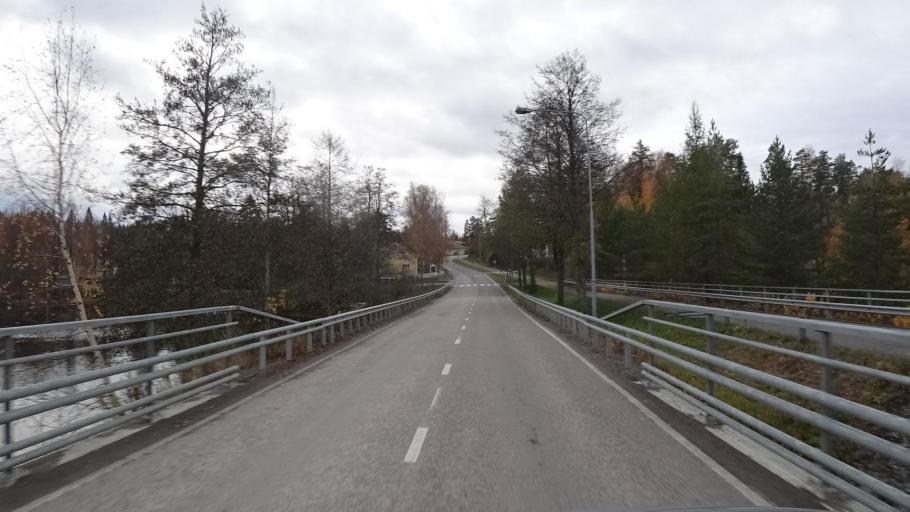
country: FI
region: Central Finland
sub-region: Joutsa
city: Joutsa
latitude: 61.7375
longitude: 26.1103
